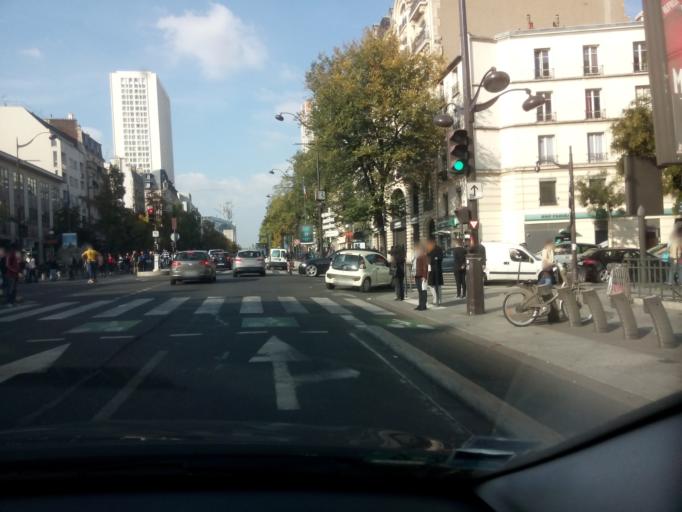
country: FR
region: Ile-de-France
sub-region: Departement du Val-de-Marne
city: Le Kremlin-Bicetre
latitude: 48.8259
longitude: 2.3574
